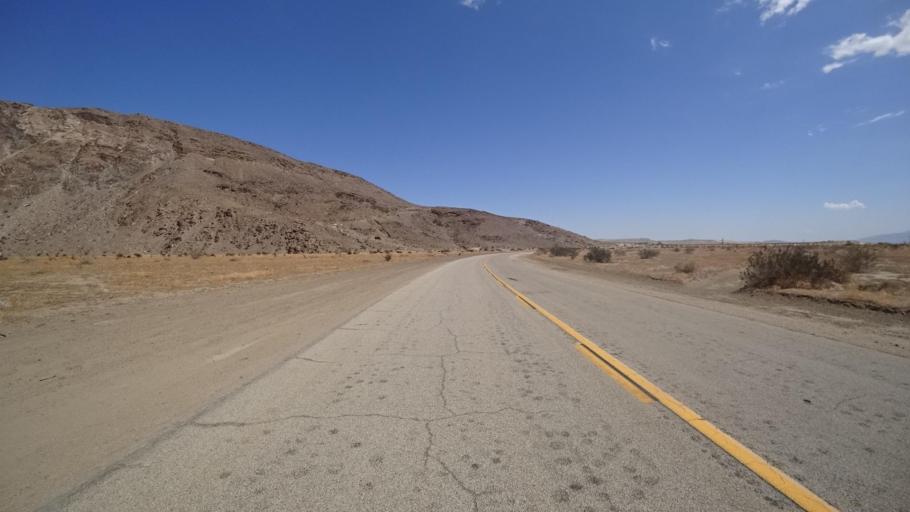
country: US
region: California
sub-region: San Diego County
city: Borrego Springs
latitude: 33.3008
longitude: -116.3166
